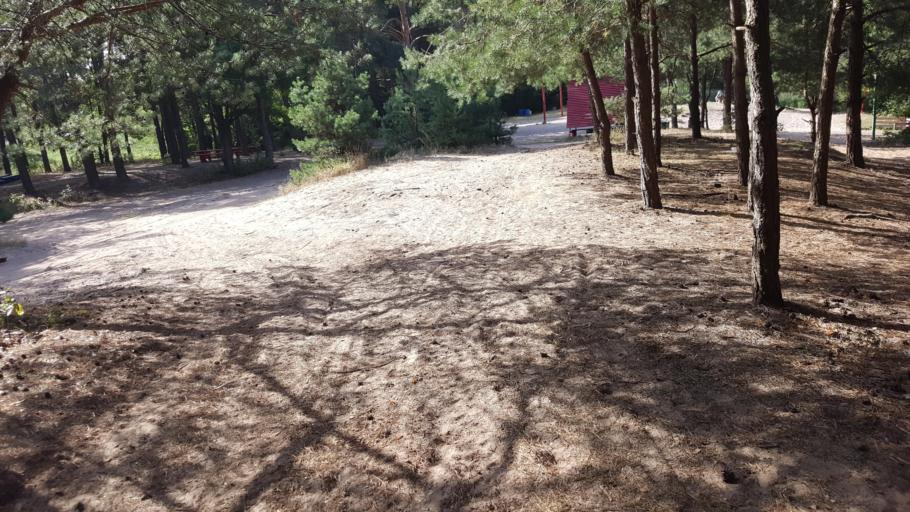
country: BY
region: Brest
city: Ivatsevichy
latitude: 52.7929
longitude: 25.5597
